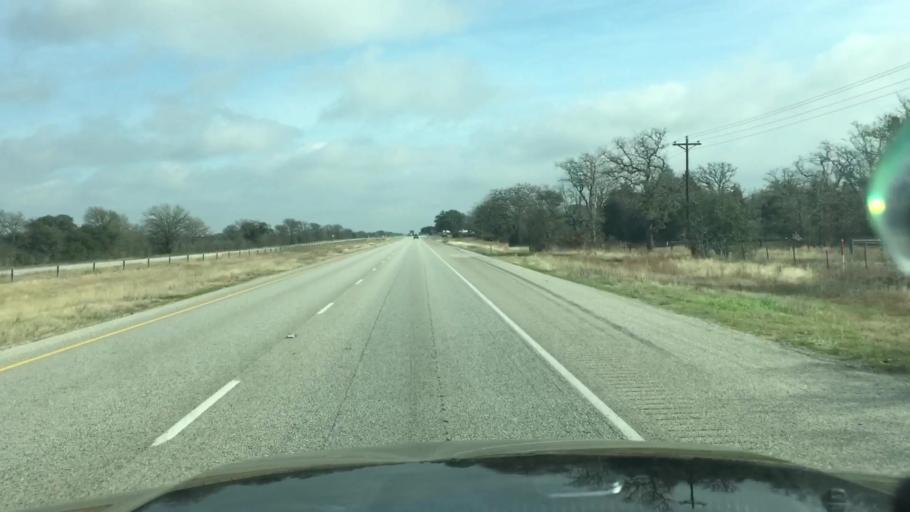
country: US
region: Texas
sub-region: Lee County
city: Giddings
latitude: 30.1736
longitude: -96.8820
